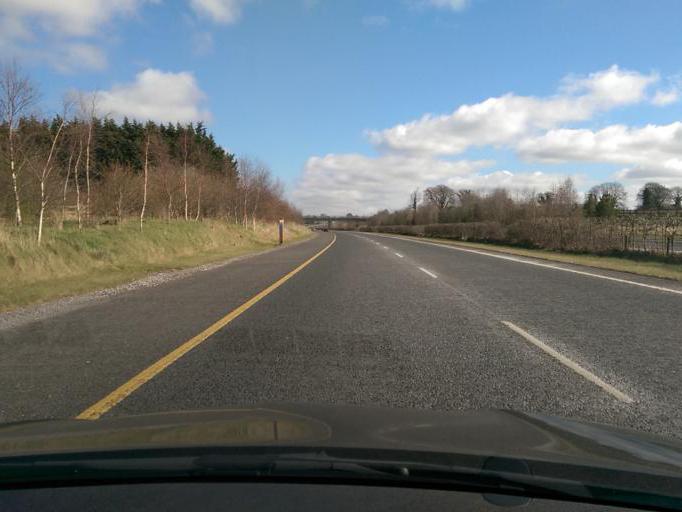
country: IE
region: Leinster
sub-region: An Mhi
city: Enfield
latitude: 53.4062
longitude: -6.7906
